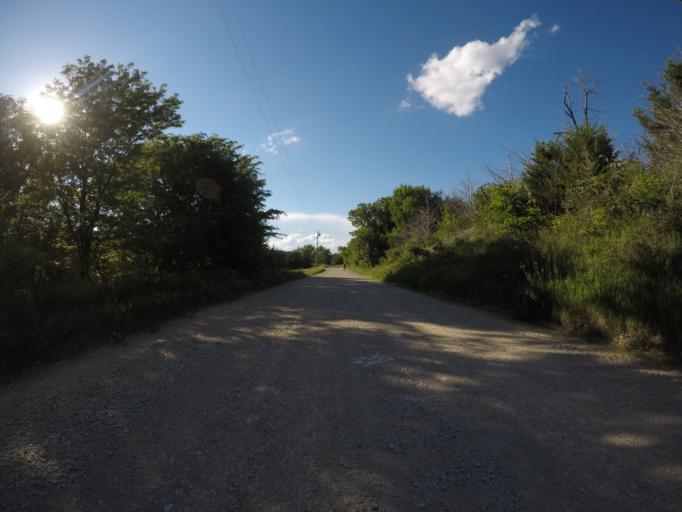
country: US
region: Kansas
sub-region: Riley County
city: Ogden
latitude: 39.2356
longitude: -96.7266
